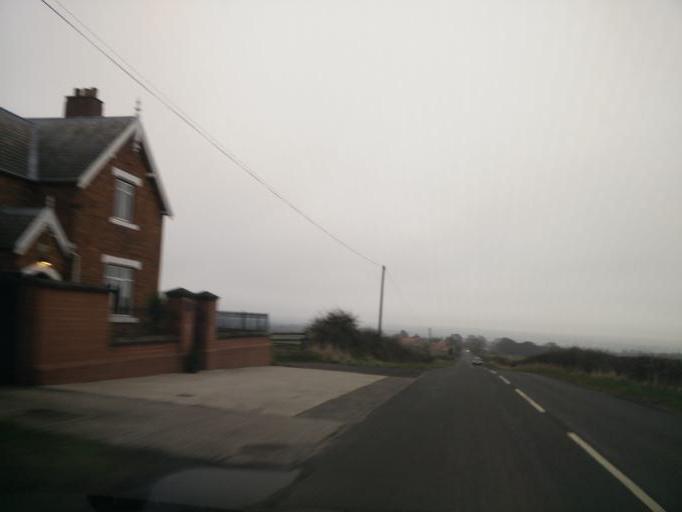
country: GB
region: England
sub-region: County Durham
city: Ushaw Moor
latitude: 54.7317
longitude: -1.6801
